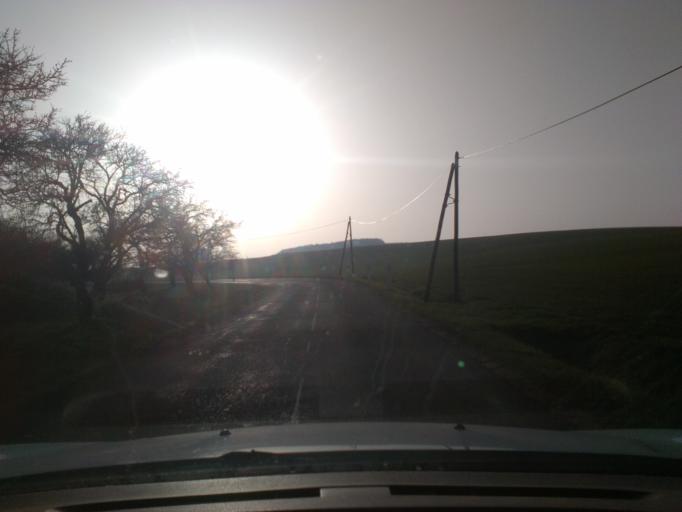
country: FR
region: Lorraine
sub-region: Departement des Vosges
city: Vittel
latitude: 48.2749
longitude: 6.0237
